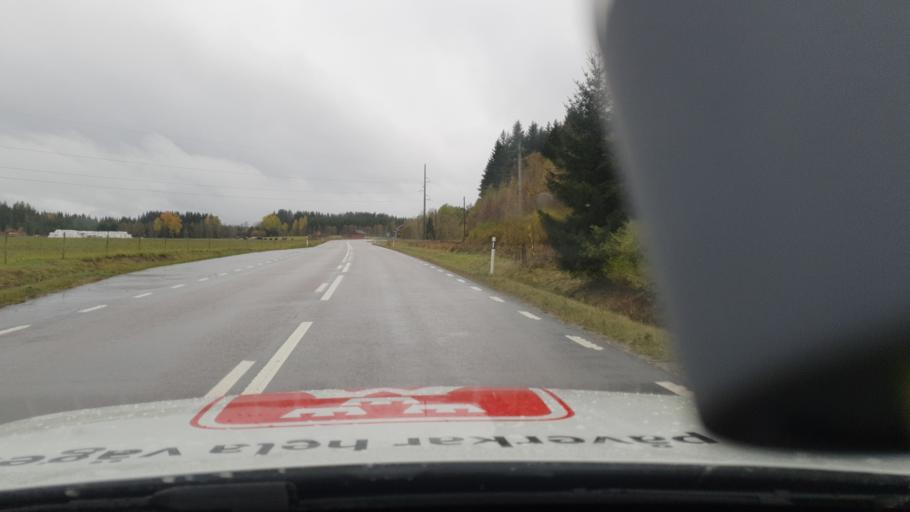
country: SE
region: Vaestra Goetaland
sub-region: Dals-Ed Kommun
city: Ed
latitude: 58.8897
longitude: 11.9180
